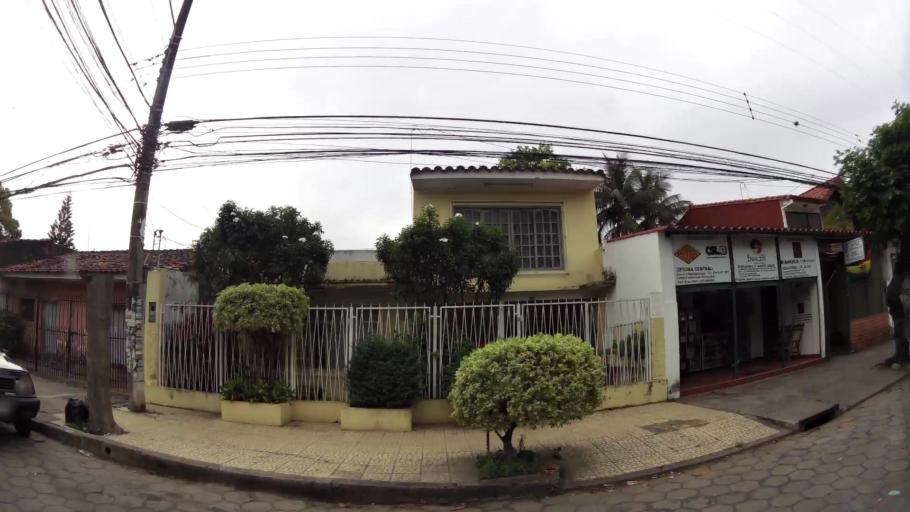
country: BO
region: Santa Cruz
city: Santa Cruz de la Sierra
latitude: -17.7889
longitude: -63.1894
